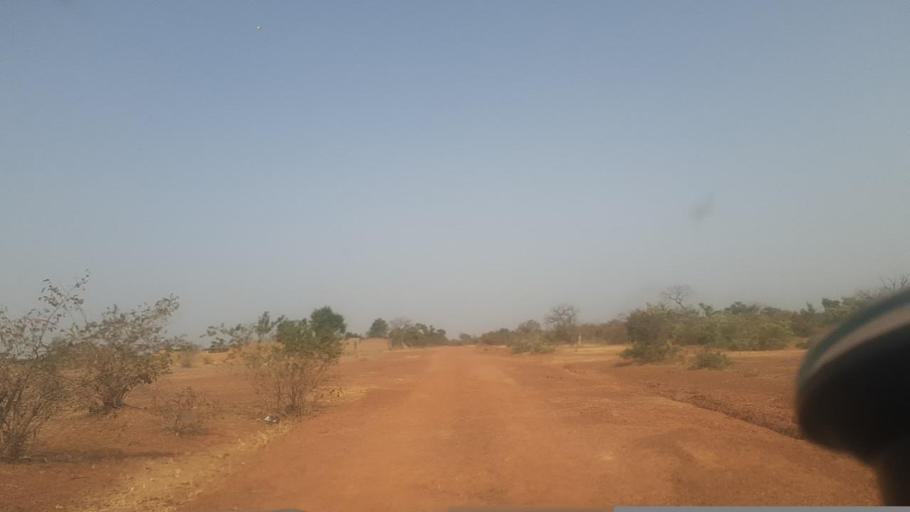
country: ML
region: Segou
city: Bla
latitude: 12.8569
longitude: -5.9728
